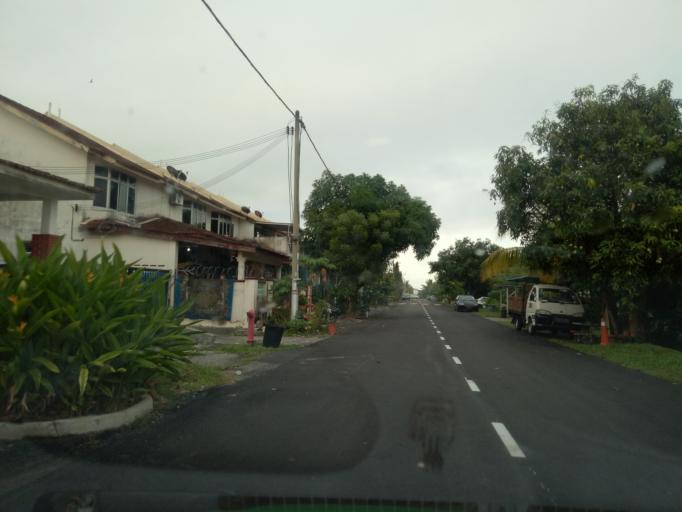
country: MY
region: Selangor
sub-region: Hulu Langat
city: Semenyih
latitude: 2.9319
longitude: 101.8622
